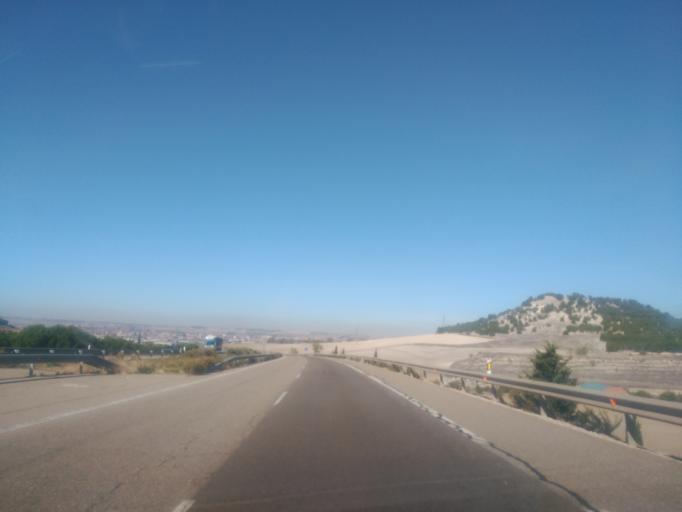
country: ES
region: Castille and Leon
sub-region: Provincia de Valladolid
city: Cisterniga
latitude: 41.6128
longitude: -4.6727
